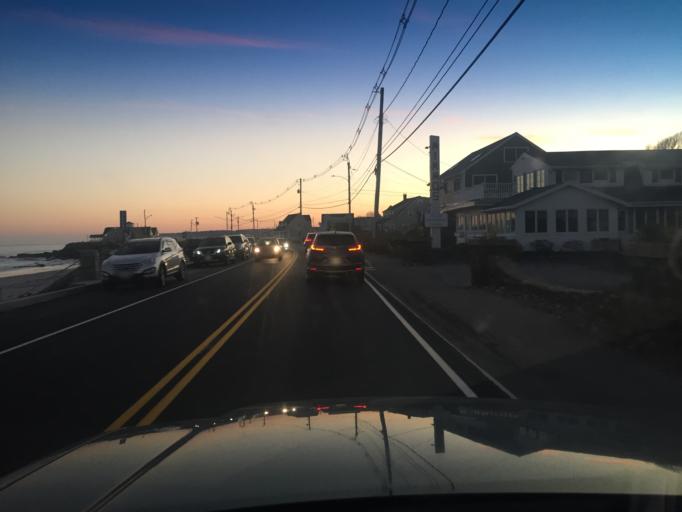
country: US
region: Maine
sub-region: York County
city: York Beach
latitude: 43.1610
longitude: -70.6208
